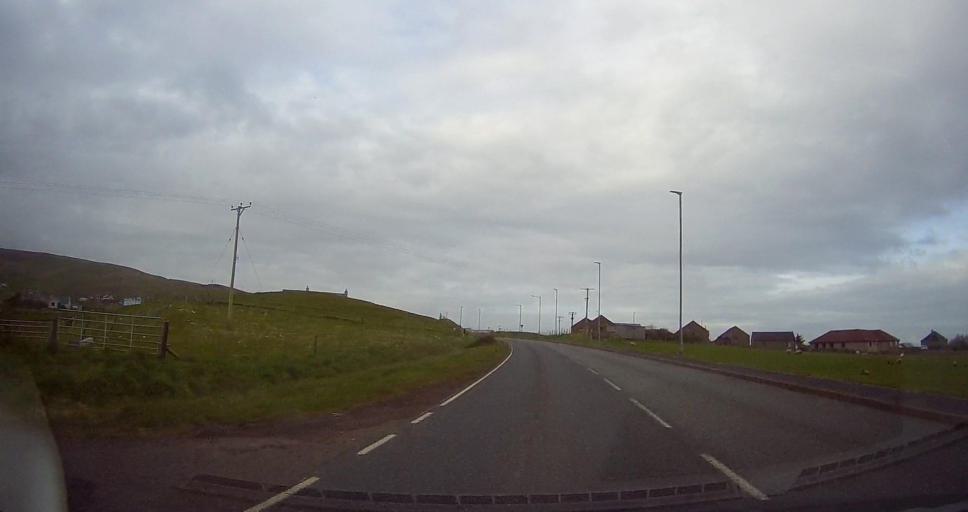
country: GB
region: Scotland
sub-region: Shetland Islands
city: Sandwick
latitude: 60.0369
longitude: -1.2302
